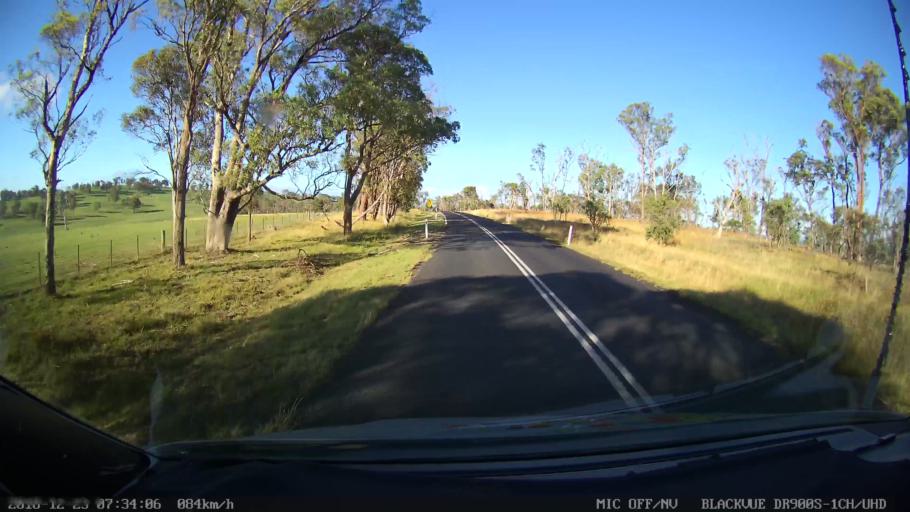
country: AU
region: New South Wales
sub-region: Armidale Dumaresq
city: Enmore
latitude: -30.5176
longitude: 152.0968
